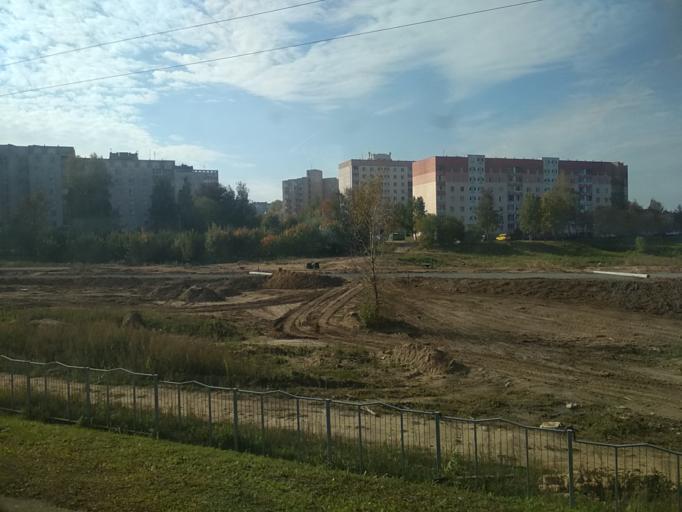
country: BY
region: Minsk
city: Syenitsa
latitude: 53.8545
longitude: 27.5574
